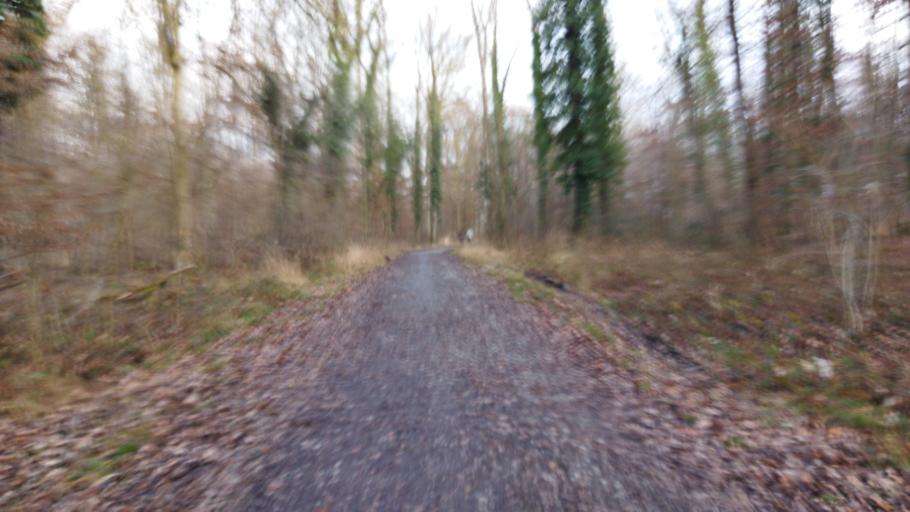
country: DE
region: Baden-Wuerttemberg
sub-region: Regierungsbezirk Stuttgart
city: Hessigheim
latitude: 48.9870
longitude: 9.1949
